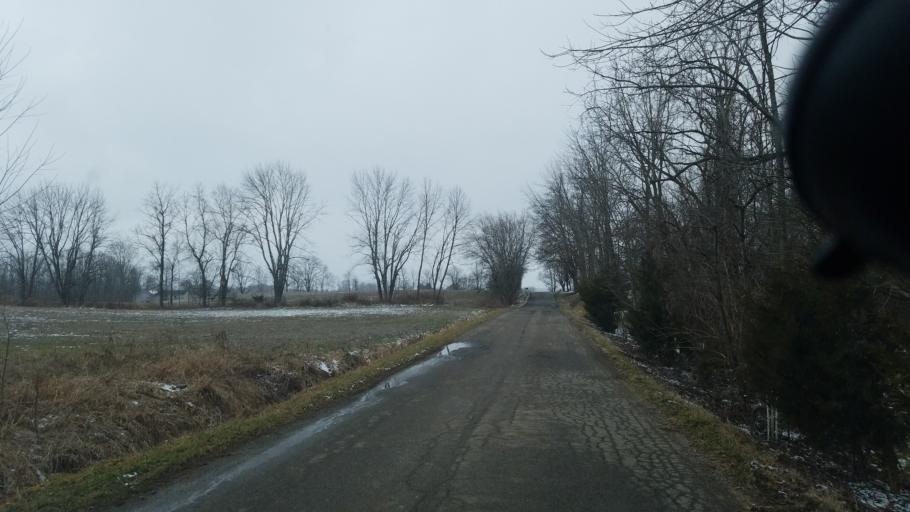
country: US
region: Ohio
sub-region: Morrow County
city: Mount Gilead
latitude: 40.5017
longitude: -82.6999
